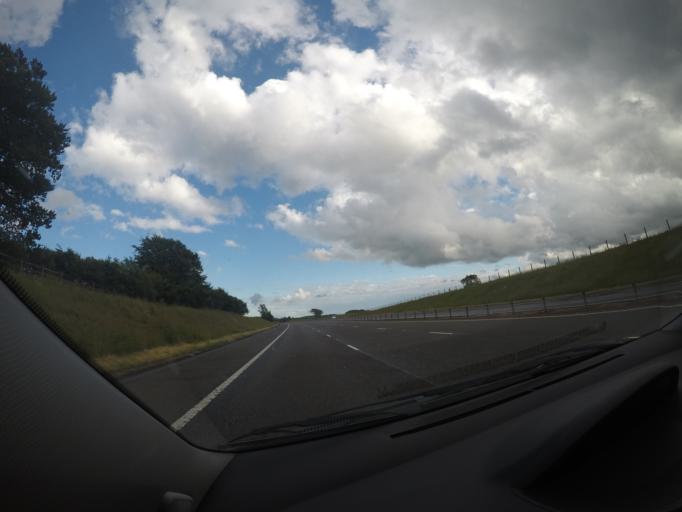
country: GB
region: Scotland
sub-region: Dumfries and Galloway
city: Lockerbie
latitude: 55.1079
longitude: -3.3533
